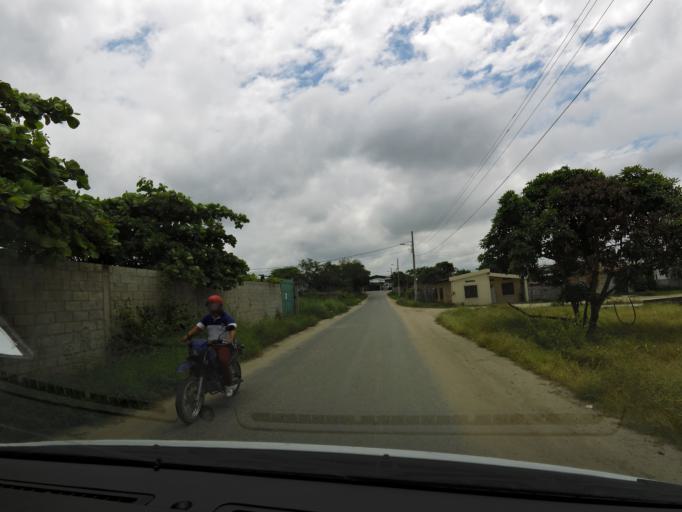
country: EC
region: El Oro
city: Huaquillas
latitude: -3.4871
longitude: -80.2113
